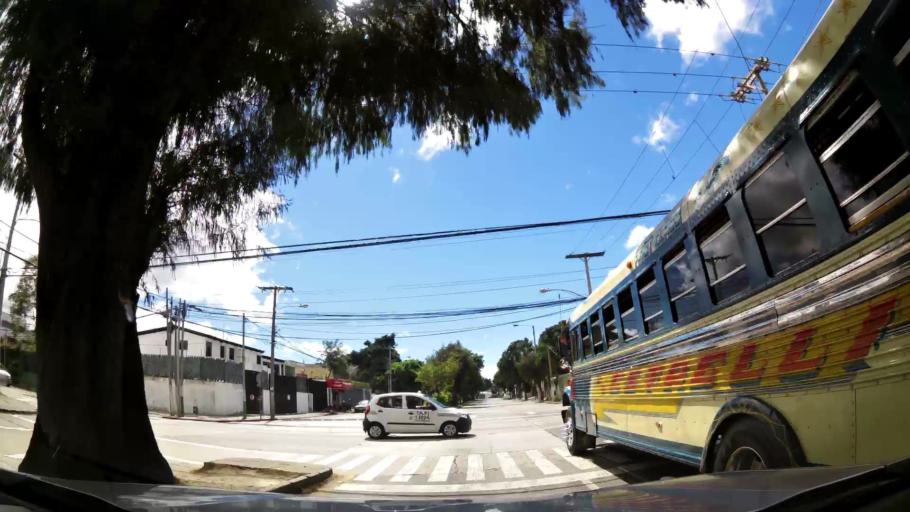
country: GT
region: Guatemala
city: Guatemala City
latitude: 14.6006
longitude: -90.5221
